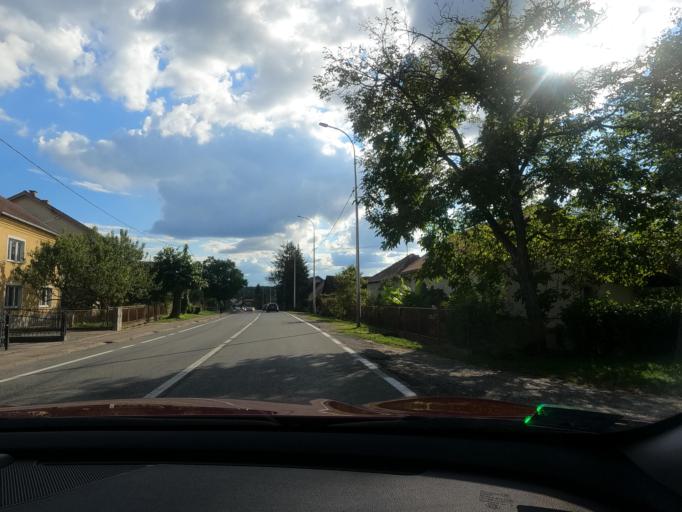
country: HR
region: Sisacko-Moslavacka
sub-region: Grad Sisak
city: Sisak
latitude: 45.4482
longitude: 16.3693
